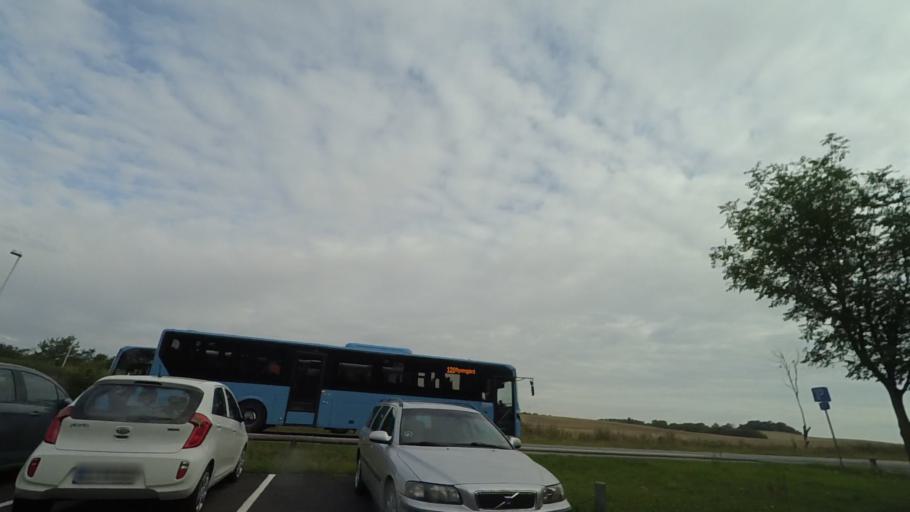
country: DK
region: Central Jutland
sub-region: Arhus Kommune
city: Logten
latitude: 56.2906
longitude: 10.3347
